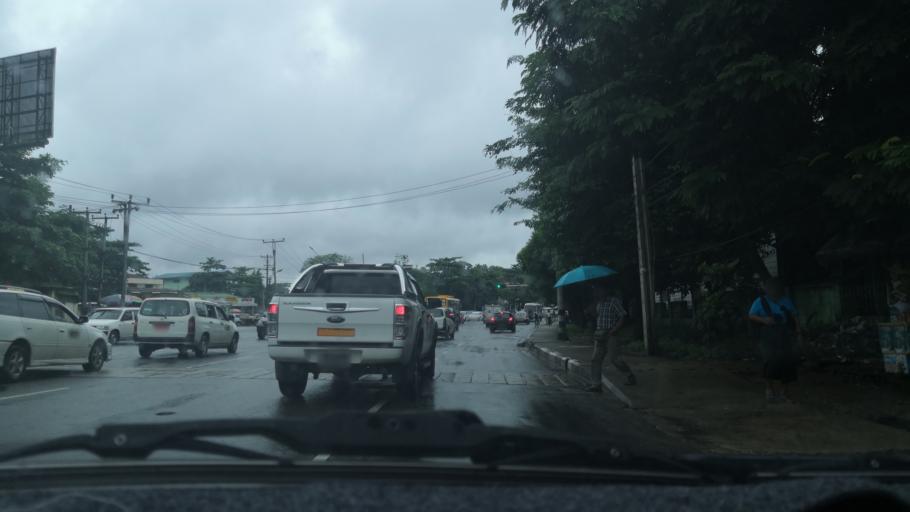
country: MM
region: Yangon
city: Yangon
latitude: 16.8922
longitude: 96.1200
